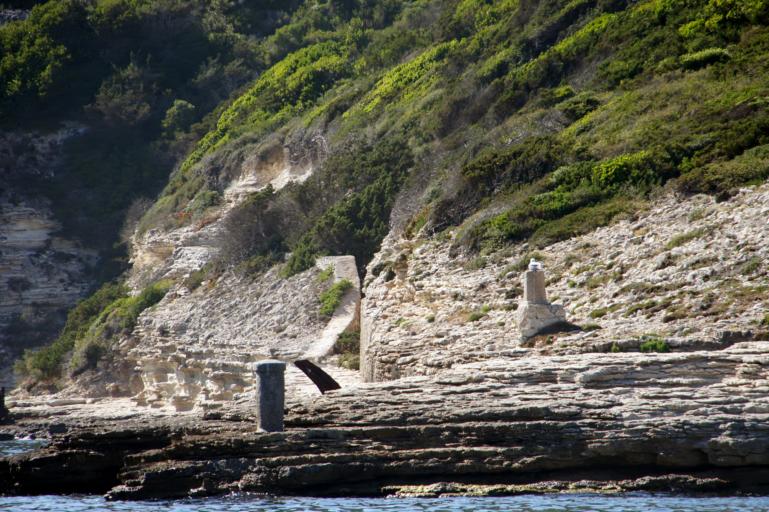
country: FR
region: Corsica
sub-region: Departement de la Corse-du-Sud
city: Bonifacio
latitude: 41.3879
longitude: 9.1482
